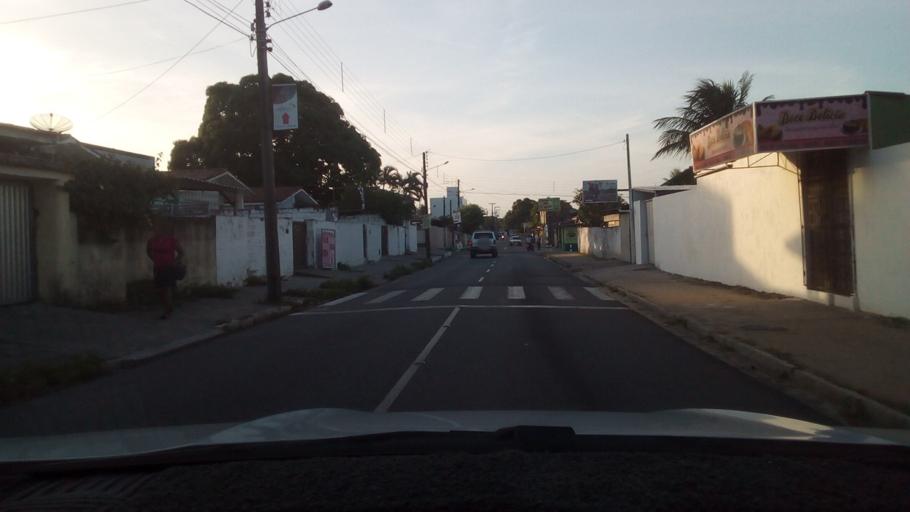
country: BR
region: Paraiba
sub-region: Bayeux
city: Bayeux
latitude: -7.1749
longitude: -34.9162
